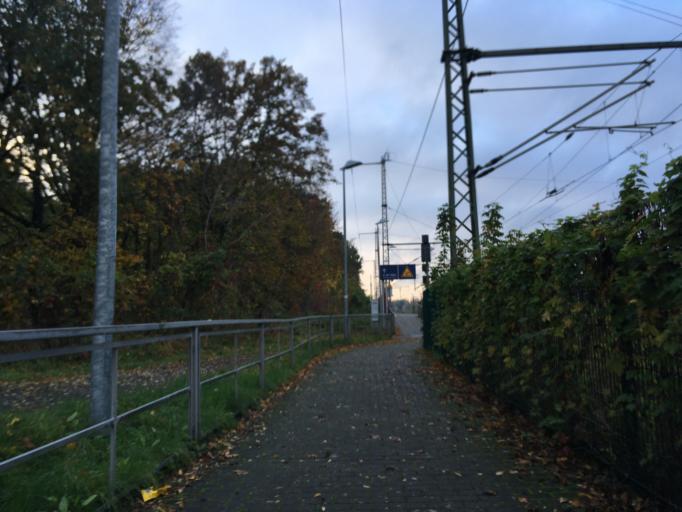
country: DE
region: Brandenburg
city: Furstenwalde
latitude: 52.3674
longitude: 14.0569
